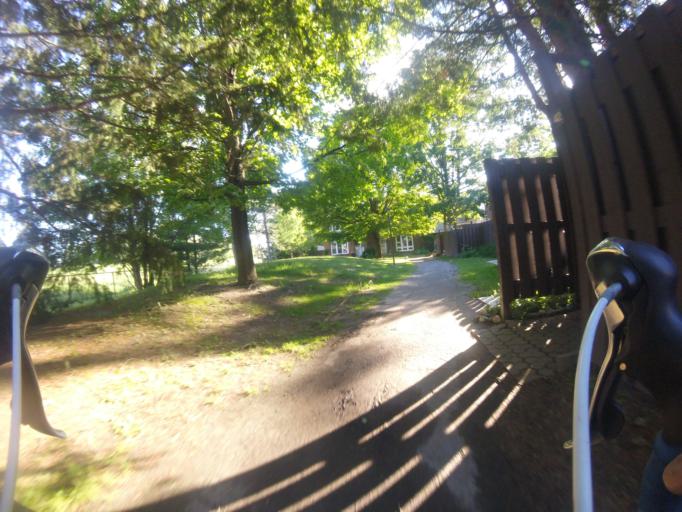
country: CA
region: Ontario
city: Bells Corners
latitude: 45.3229
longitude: -75.7788
